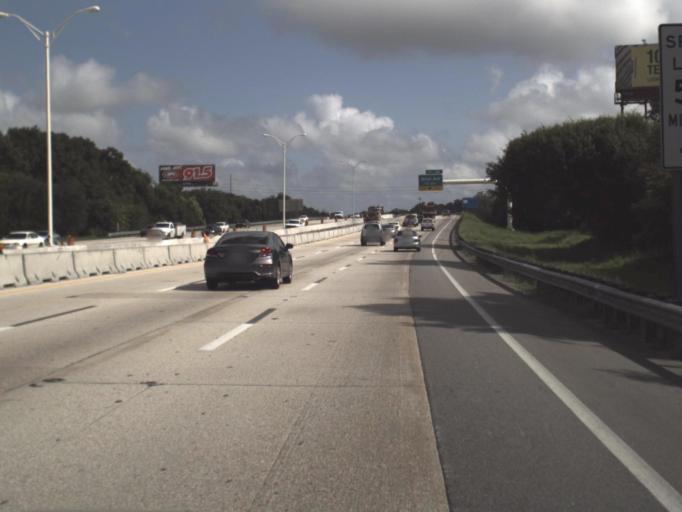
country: US
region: Florida
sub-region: Hillsborough County
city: Tampa
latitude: 28.0004
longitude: -82.4535
